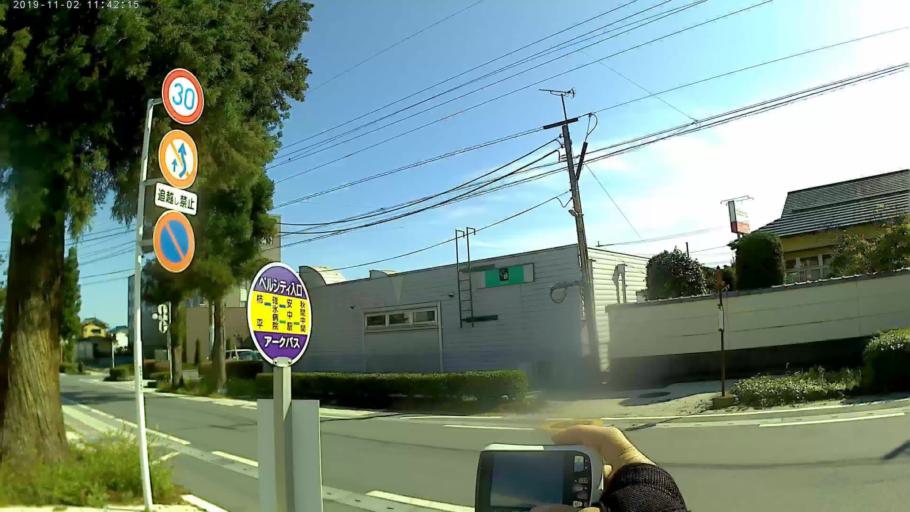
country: JP
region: Gunma
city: Annaka
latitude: 36.3195
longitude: 138.8741
